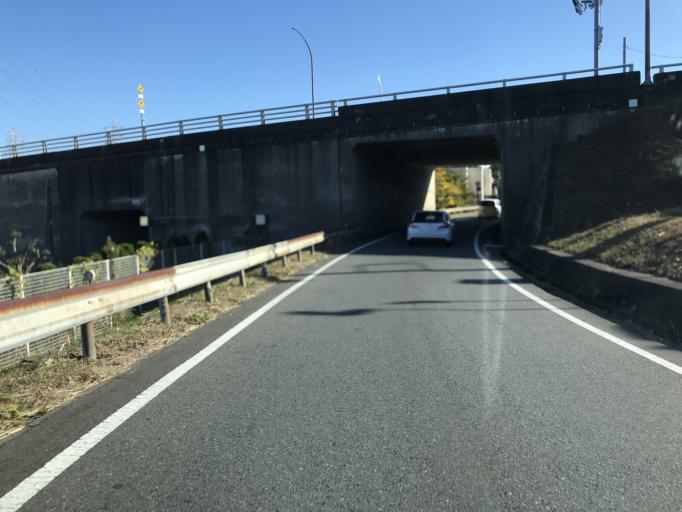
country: JP
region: Aichi
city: Kanie
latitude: 35.1406
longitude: 136.8358
